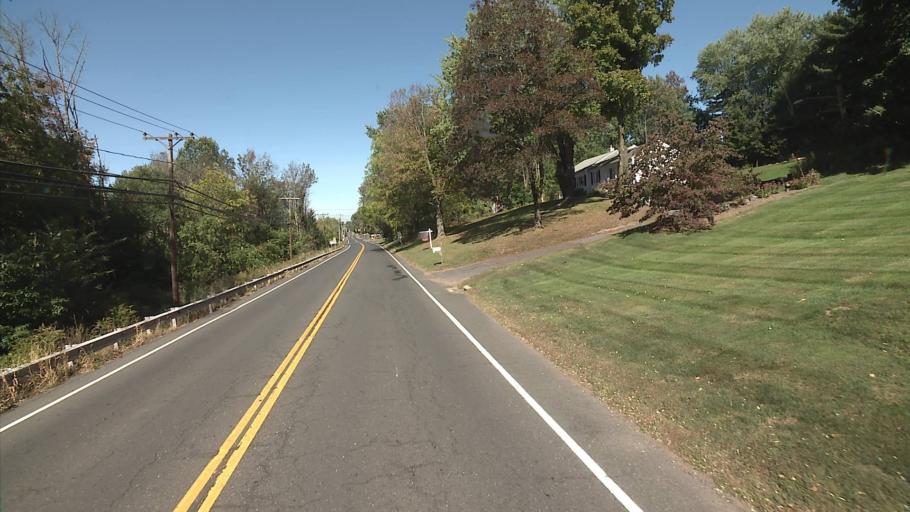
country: US
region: Connecticut
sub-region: Tolland County
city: Ellington
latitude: 41.9087
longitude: -72.4550
